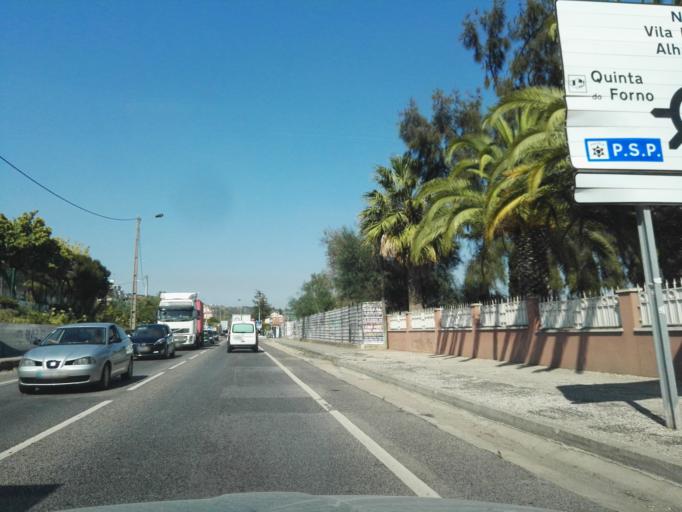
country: PT
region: Lisbon
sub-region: Vila Franca de Xira
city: Sobralinho
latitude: 38.9007
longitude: -9.0365
